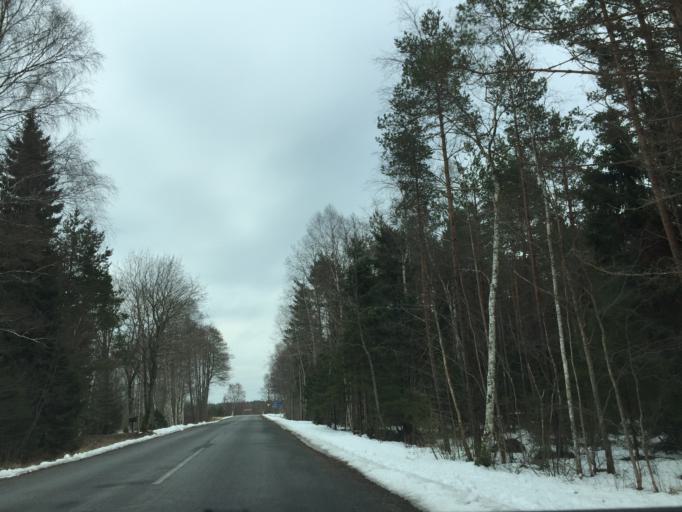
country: EE
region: Saare
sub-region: Kuressaare linn
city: Kuressaare
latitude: 58.4181
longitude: 22.1280
